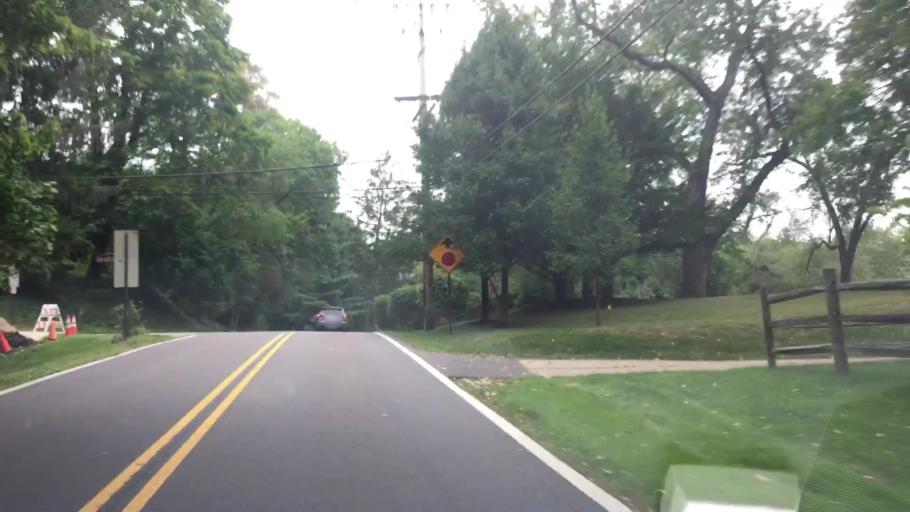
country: US
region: Pennsylvania
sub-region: Allegheny County
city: Carnegie
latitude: 40.4253
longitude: -80.0940
